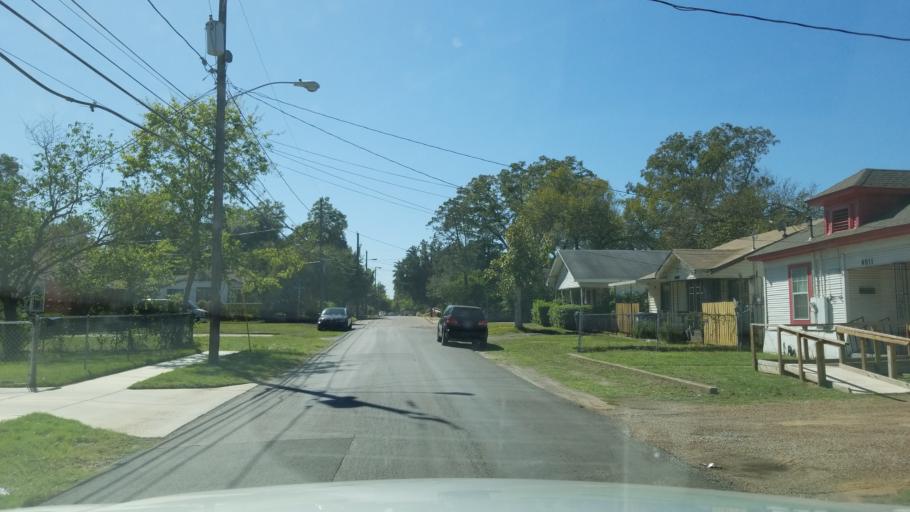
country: US
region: Texas
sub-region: Dallas County
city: Dallas
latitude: 32.7726
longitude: -96.7487
